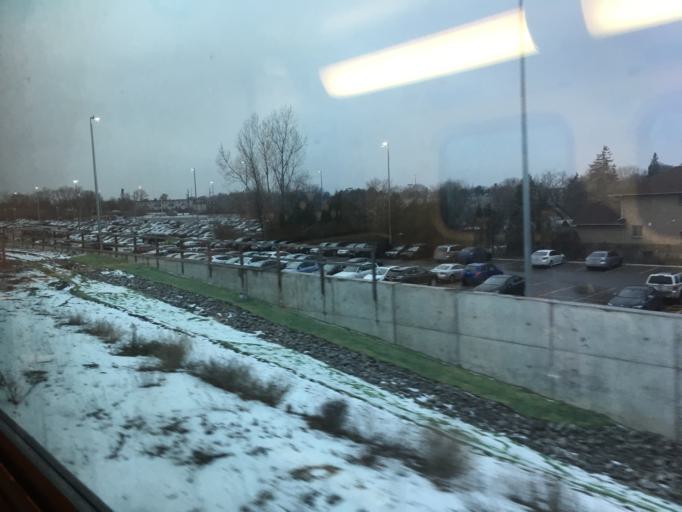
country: CA
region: Ontario
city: Scarborough
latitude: 43.7554
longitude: -79.1960
